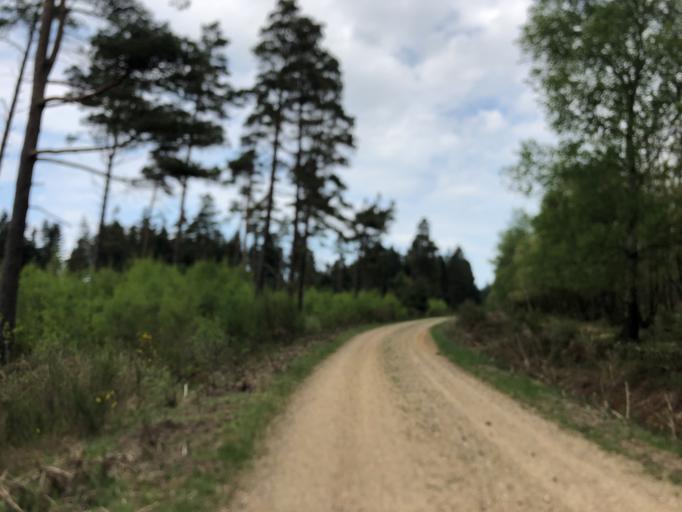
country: DK
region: Central Jutland
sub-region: Holstebro Kommune
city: Ulfborg
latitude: 56.2806
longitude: 8.4331
